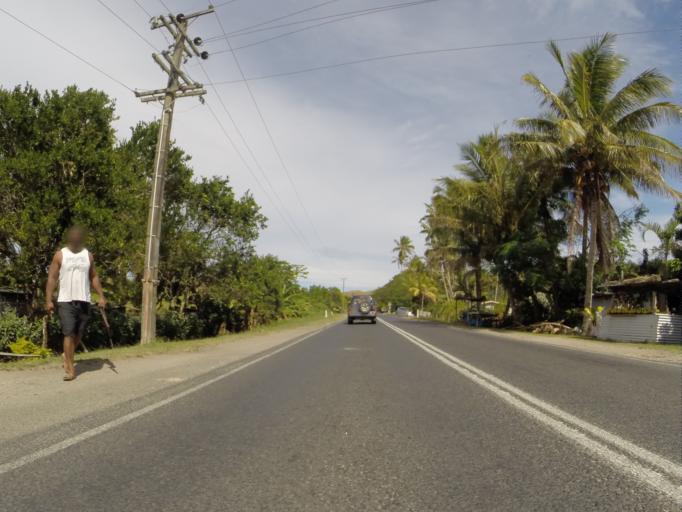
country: FJ
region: Western
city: Nadi
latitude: -18.1591
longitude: 177.4891
